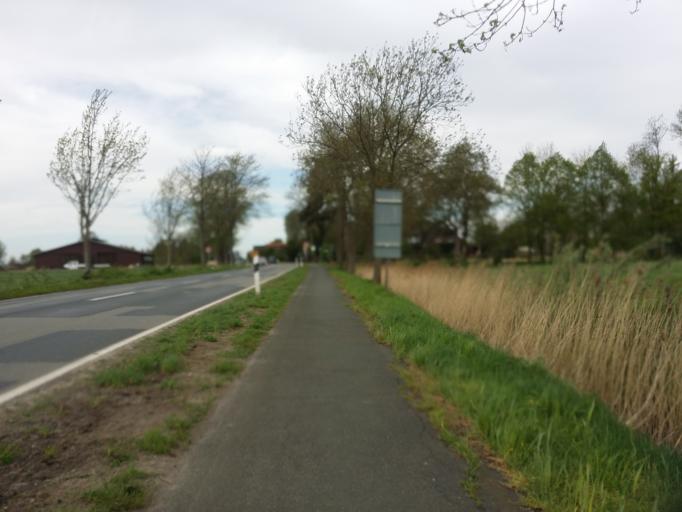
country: DE
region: Lower Saxony
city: Lemwerder
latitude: 53.1453
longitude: 8.5547
